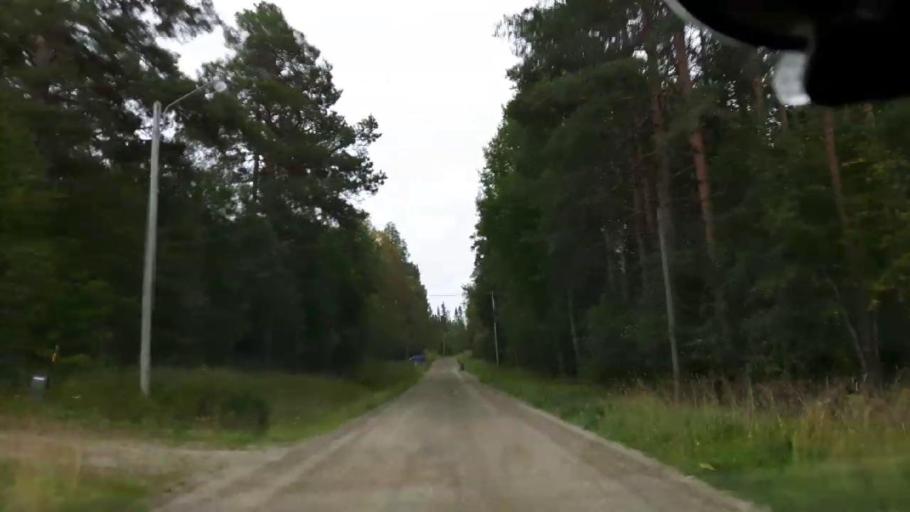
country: SE
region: Jaemtland
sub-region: Braecke Kommun
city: Braecke
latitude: 63.0303
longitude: 15.3710
